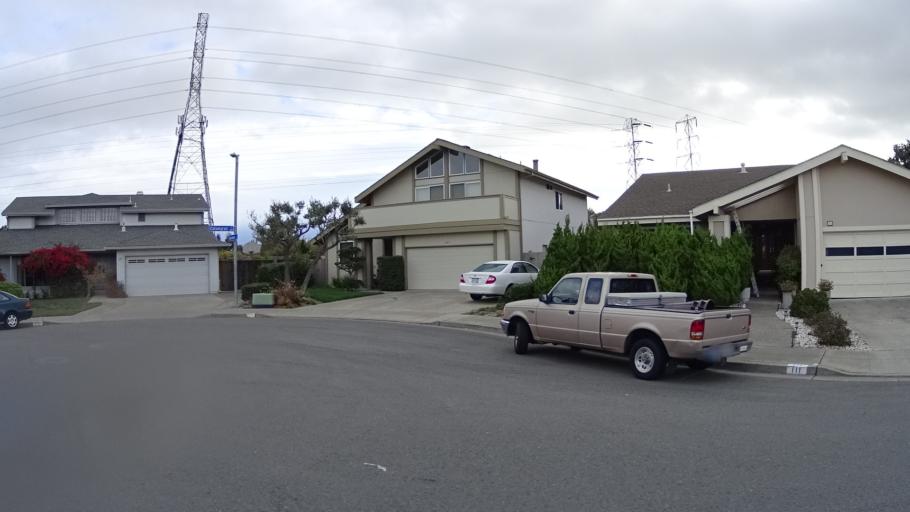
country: US
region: California
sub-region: San Mateo County
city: Foster City
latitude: 37.5523
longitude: -122.2553
